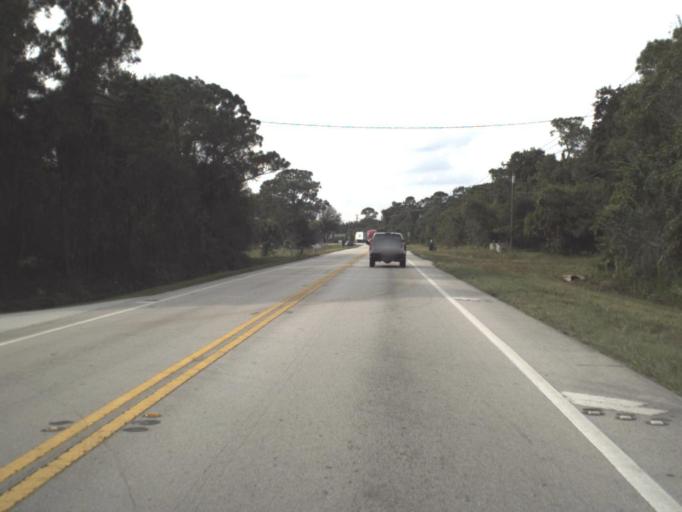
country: US
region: Florida
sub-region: Okeechobee County
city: Cypress Quarters
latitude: 27.2450
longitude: -80.7960
